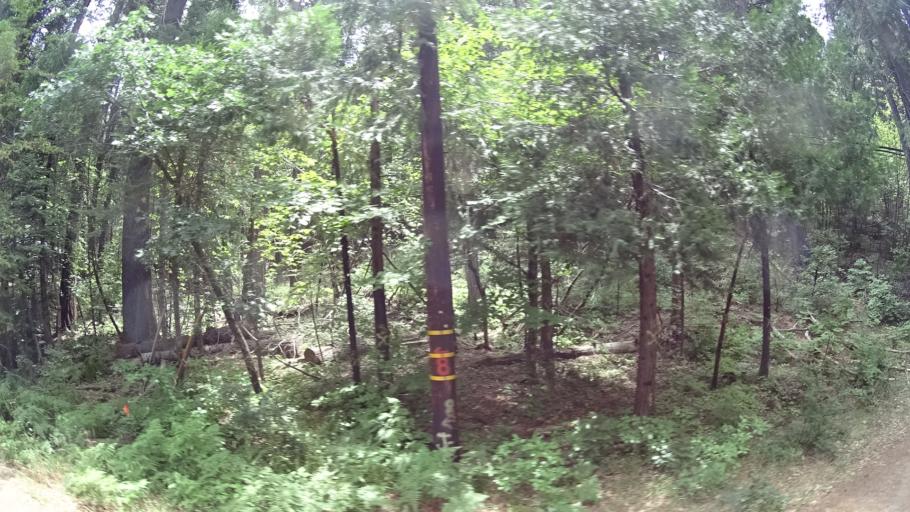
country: US
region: California
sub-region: Calaveras County
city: Arnold
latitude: 38.2578
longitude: -120.3410
